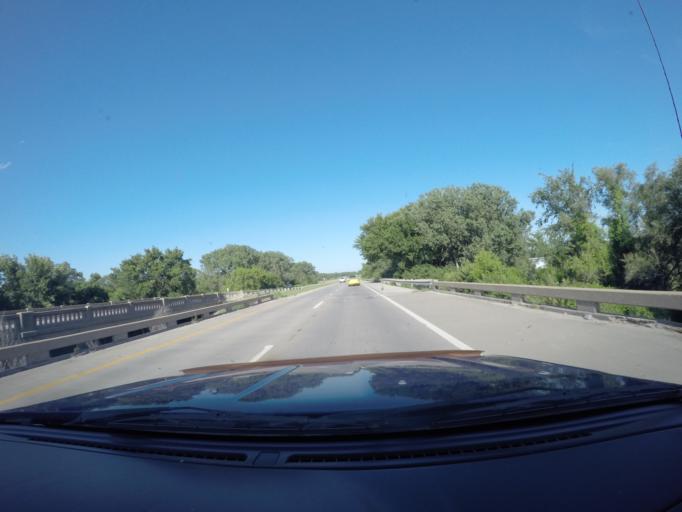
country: US
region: Kansas
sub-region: Shawnee County
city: Topeka
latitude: 39.0910
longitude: -95.6355
